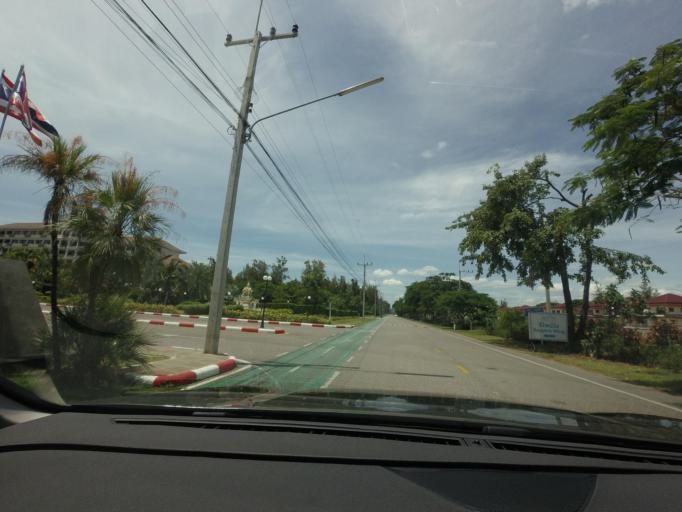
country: TH
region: Prachuap Khiri Khan
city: Hua Hin
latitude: 12.5031
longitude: 99.9727
